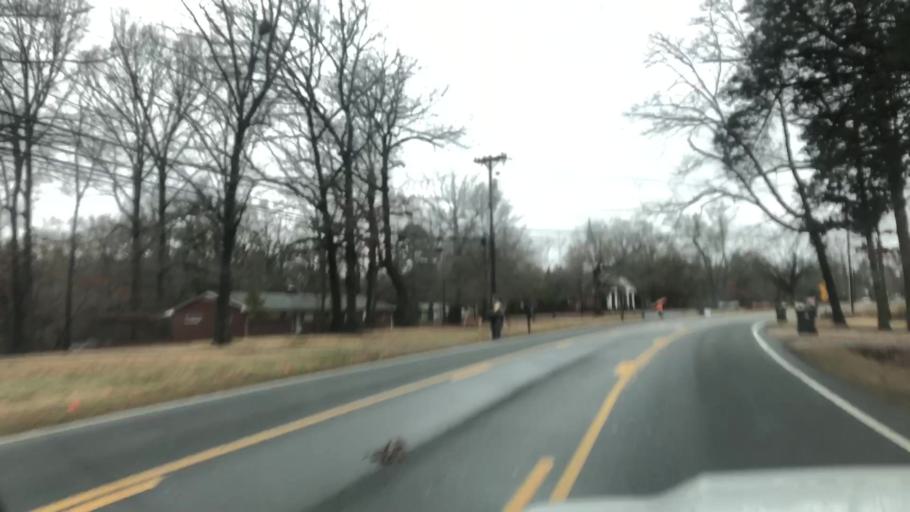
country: US
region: North Carolina
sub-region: Mecklenburg County
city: Mint Hill
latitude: 35.2381
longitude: -80.6678
